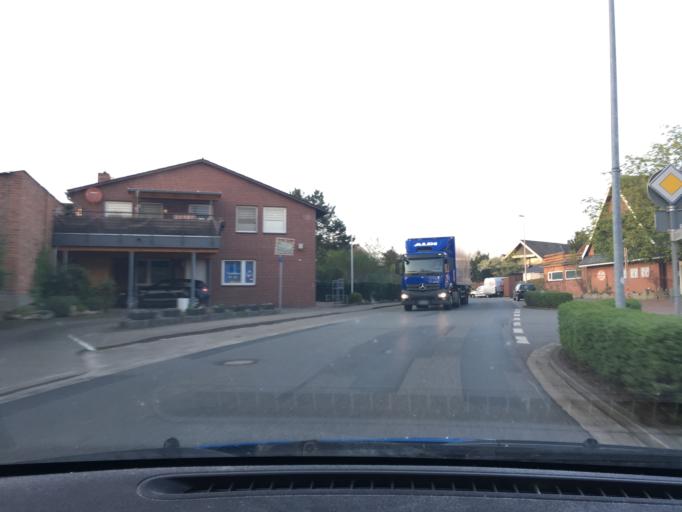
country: DE
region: Lower Saxony
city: Kirchgellersen
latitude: 53.2313
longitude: 10.2933
